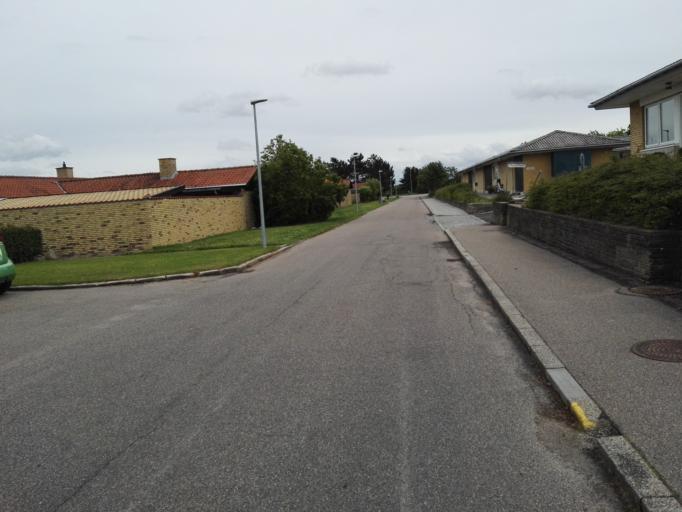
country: DK
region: Capital Region
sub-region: Egedal Kommune
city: Olstykke
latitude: 55.7752
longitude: 12.1706
